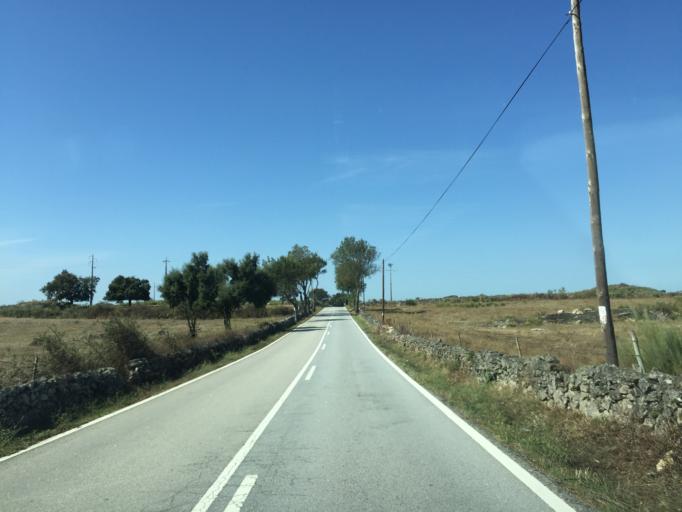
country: PT
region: Portalegre
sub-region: Castelo de Vide
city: Povoa e Meadas
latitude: 39.4393
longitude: -7.5511
